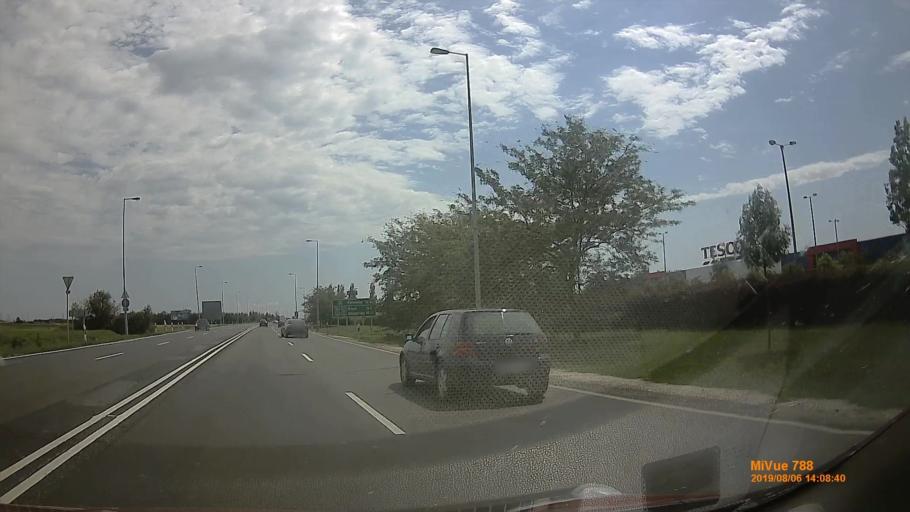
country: HU
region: Vas
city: Szombathely
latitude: 47.2405
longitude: 16.6544
